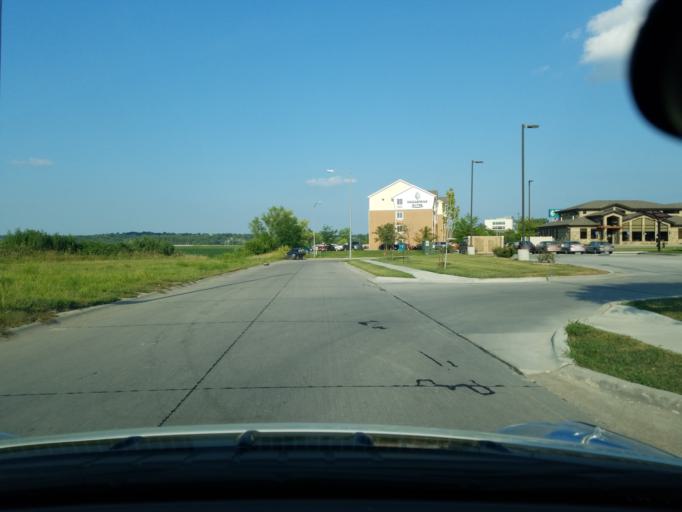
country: US
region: Nebraska
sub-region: Sarpy County
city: Offutt Air Force Base
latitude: 41.1385
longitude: -95.9554
